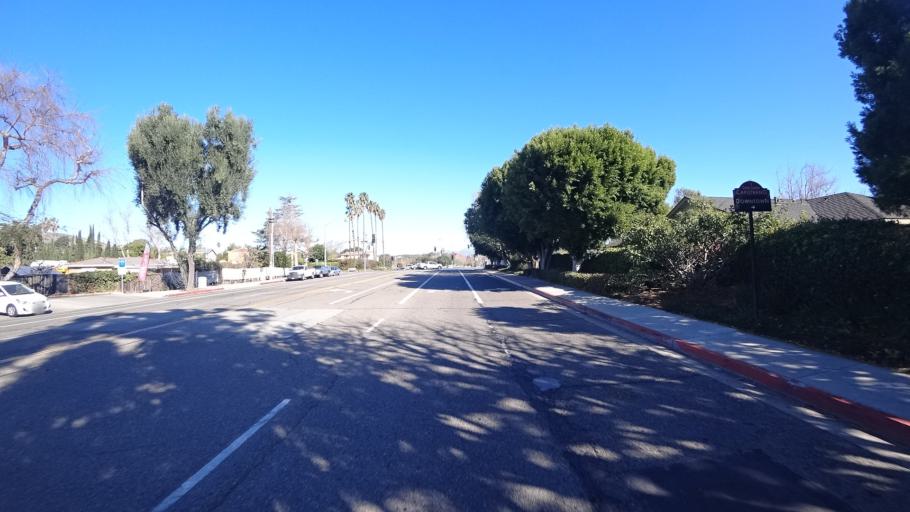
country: US
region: California
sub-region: Orange County
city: San Juan Capistrano
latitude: 33.4969
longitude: -117.6670
